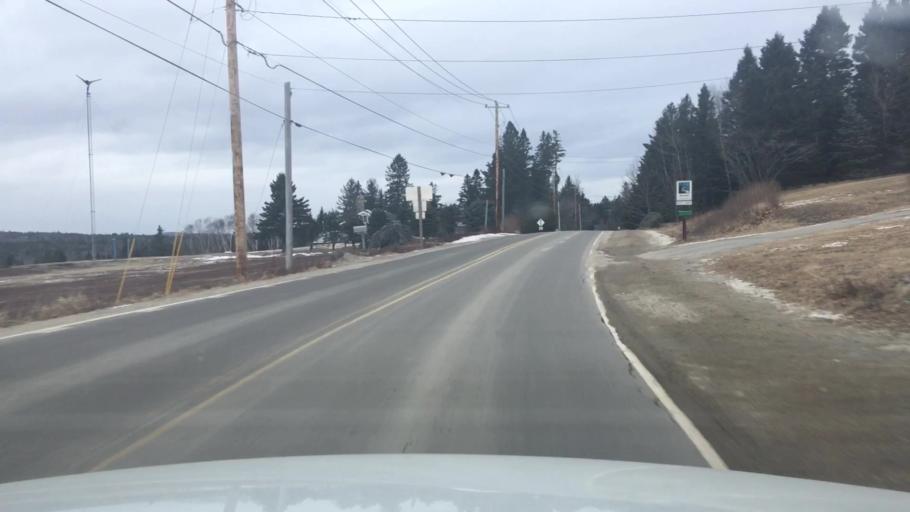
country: US
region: Maine
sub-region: Washington County
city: Addison
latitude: 44.6219
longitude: -67.7119
